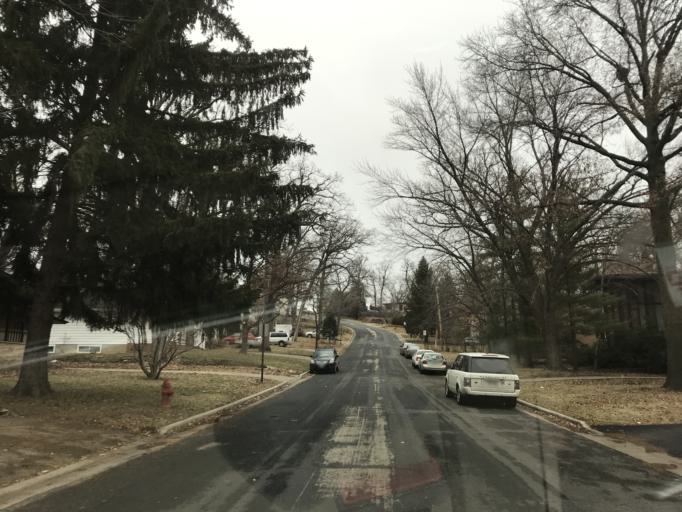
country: US
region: Wisconsin
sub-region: Dane County
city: Monona
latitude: 43.0502
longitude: -89.3265
